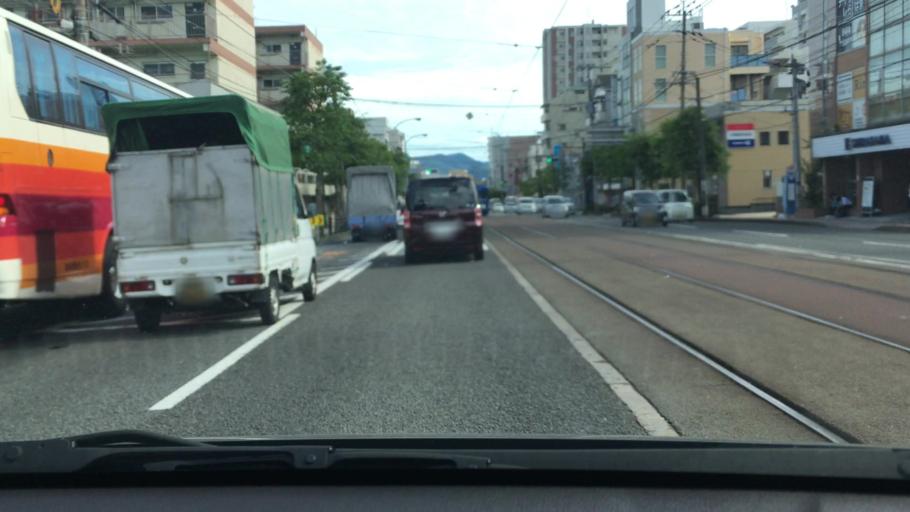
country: JP
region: Nagasaki
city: Obita
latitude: 32.7845
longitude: 129.8625
